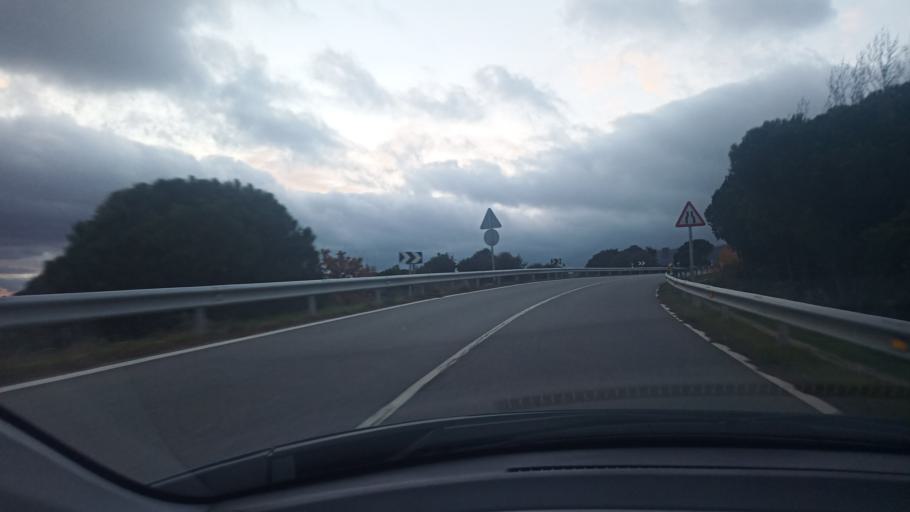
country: ES
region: Madrid
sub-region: Provincia de Madrid
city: Zarzalejo
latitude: 40.5399
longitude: -4.1506
